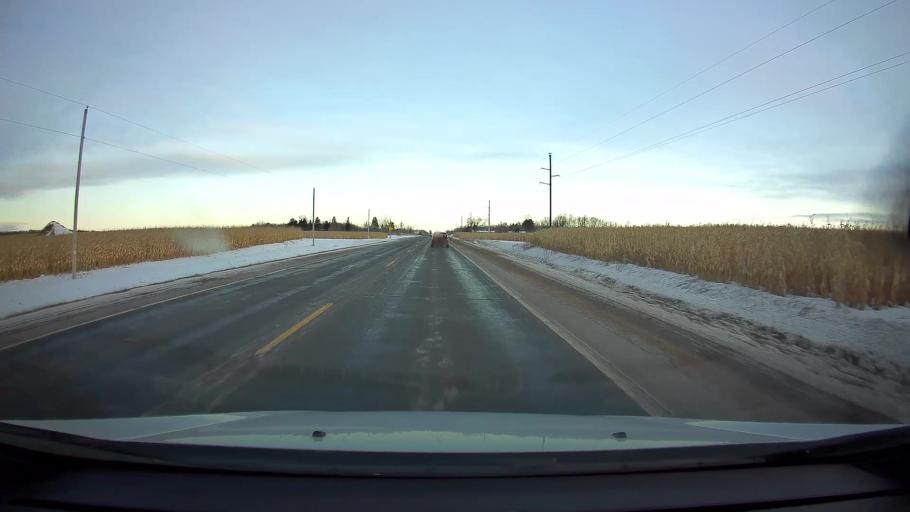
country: US
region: Wisconsin
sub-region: Barron County
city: Turtle Lake
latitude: 45.3490
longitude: -92.1668
